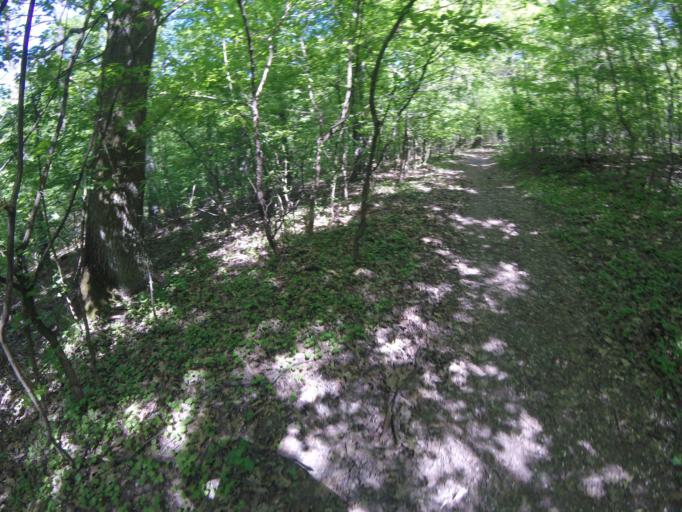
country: HU
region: Pest
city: Nagymaros
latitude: 47.7928
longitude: 18.9237
